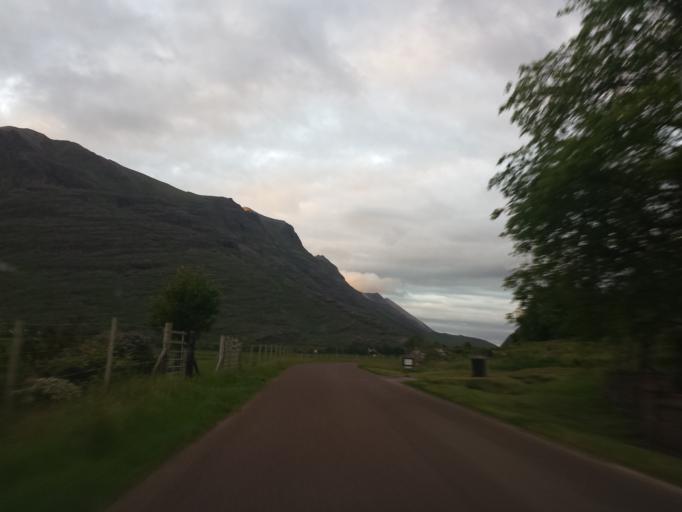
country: GB
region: Scotland
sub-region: Highland
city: Ullapool
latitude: 57.5329
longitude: -5.5143
